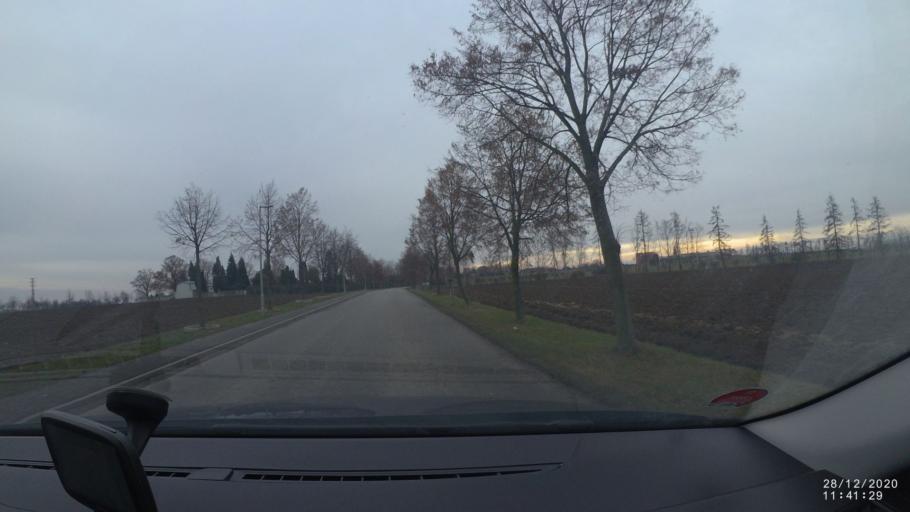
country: CZ
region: Central Bohemia
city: Zelenec
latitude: 50.1413
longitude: 14.6562
